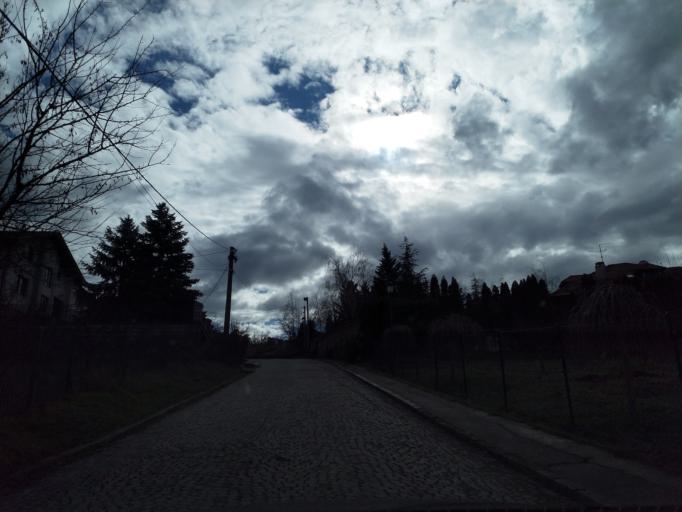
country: RS
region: Central Serbia
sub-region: Belgrade
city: Grocka
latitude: 44.6670
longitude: 20.7208
